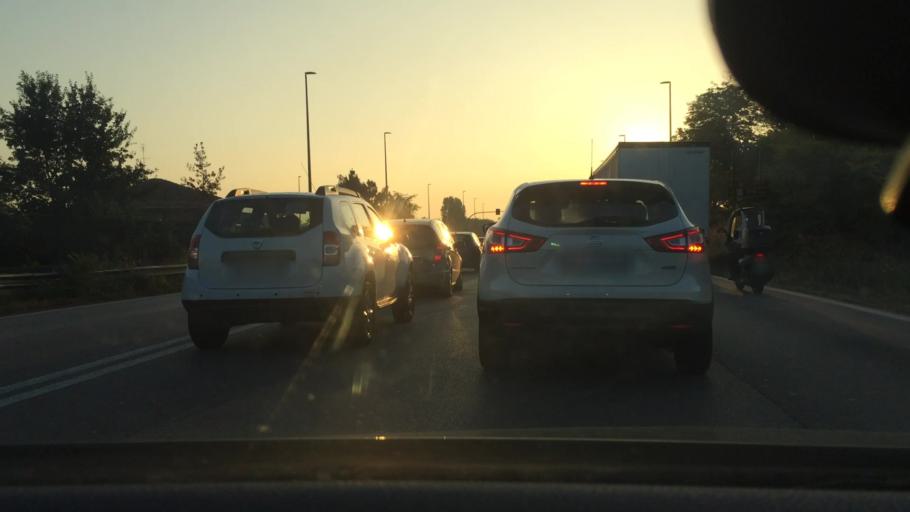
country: IT
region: Lombardy
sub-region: Citta metropolitana di Milano
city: Passirana
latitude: 45.5400
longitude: 9.0327
